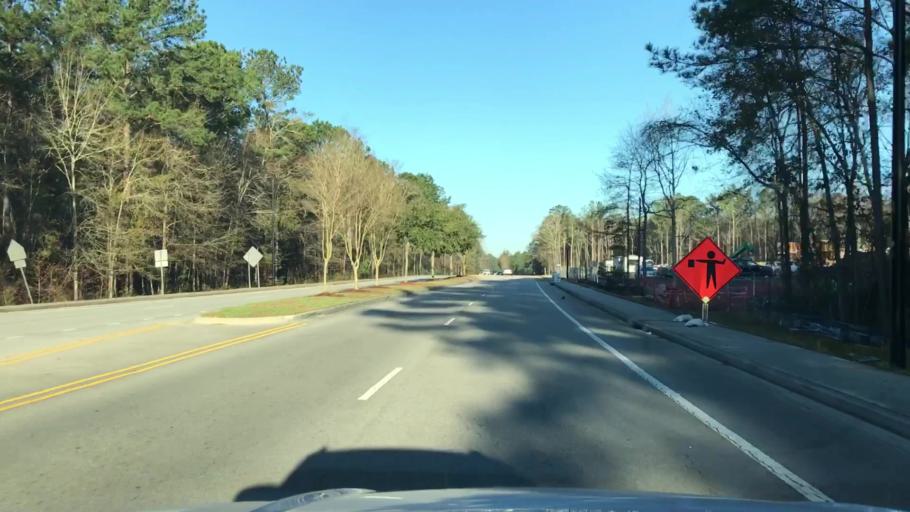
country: US
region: South Carolina
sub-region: Berkeley County
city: Ladson
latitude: 32.9229
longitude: -80.1104
